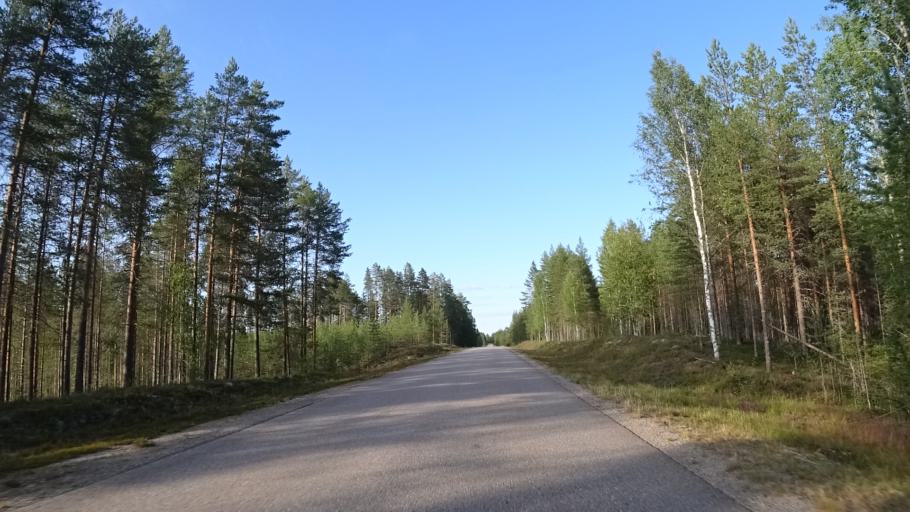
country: FI
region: North Karelia
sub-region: Joensuu
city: Eno
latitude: 63.0762
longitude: 30.5770
